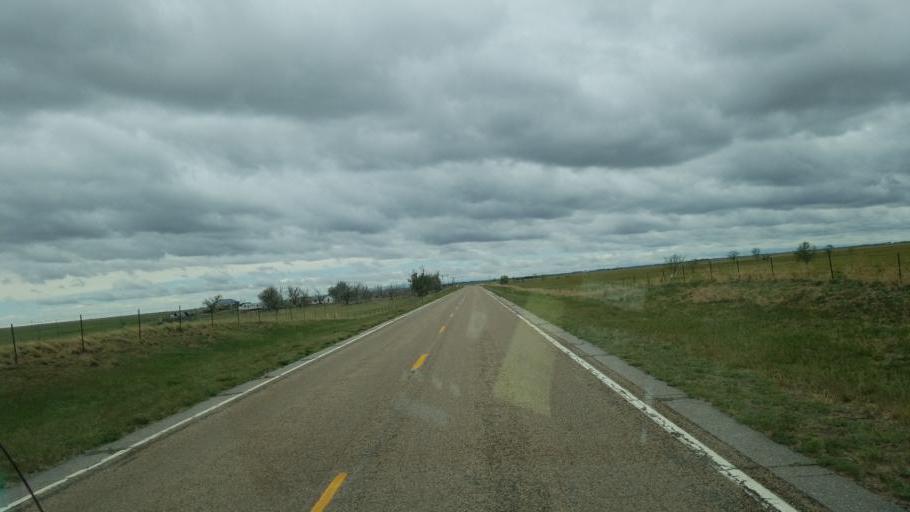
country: US
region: Colorado
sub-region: El Paso County
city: Ellicott
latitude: 38.8397
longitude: -103.9360
